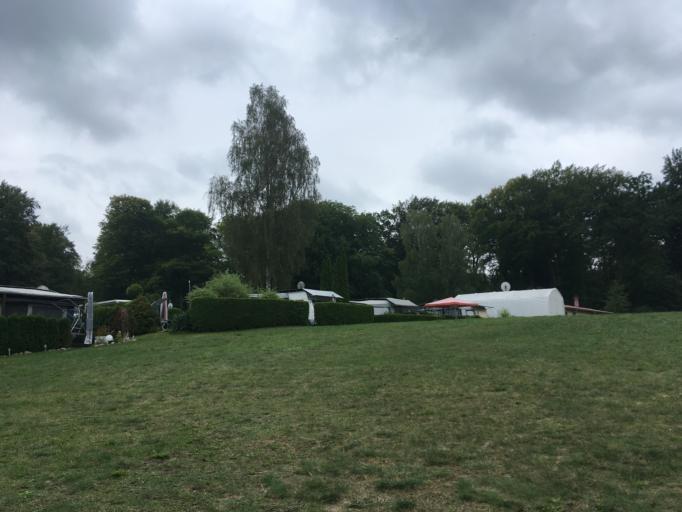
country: DE
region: Brandenburg
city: Gransee
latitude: 53.0748
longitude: 13.1752
